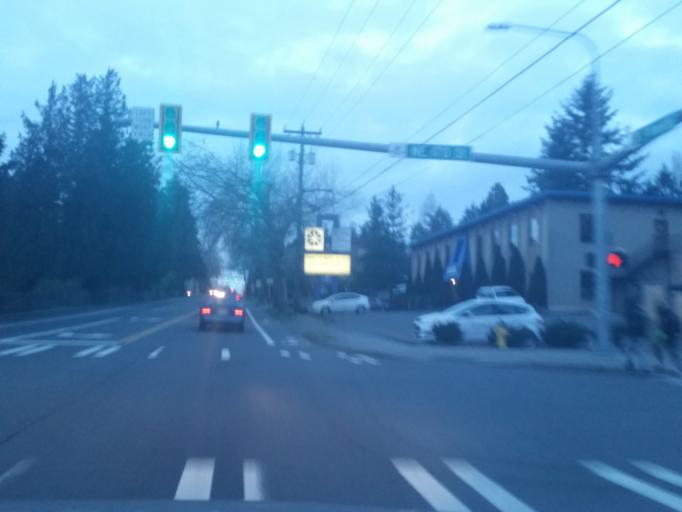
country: US
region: Washington
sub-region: King County
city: Shoreline
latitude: 47.7520
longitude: -122.3133
